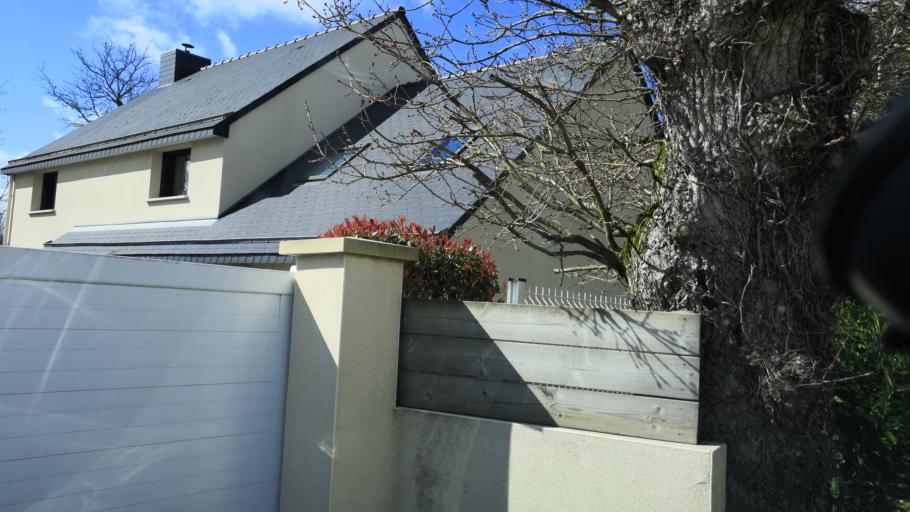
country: FR
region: Brittany
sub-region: Departement d'Ille-et-Vilaine
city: Bedee
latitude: 48.1839
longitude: -1.9470
